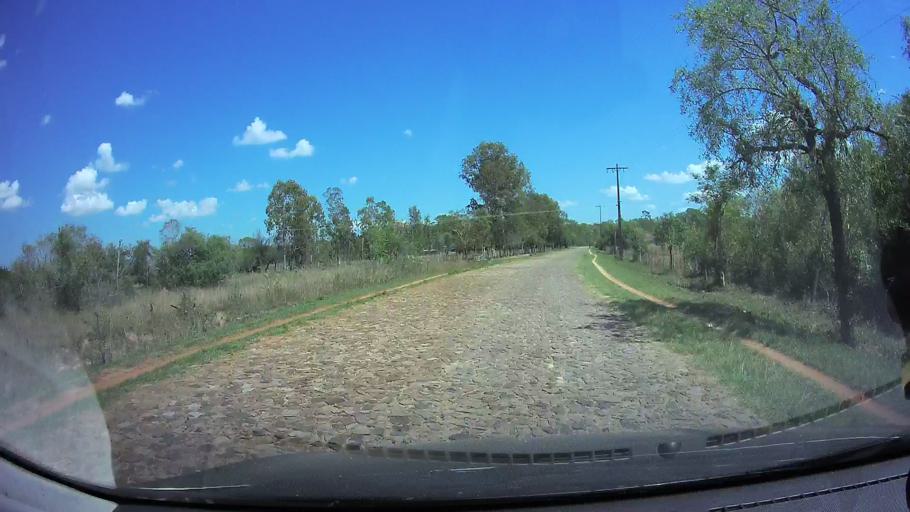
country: PY
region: Cordillera
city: Emboscada
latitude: -25.1186
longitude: -57.2799
